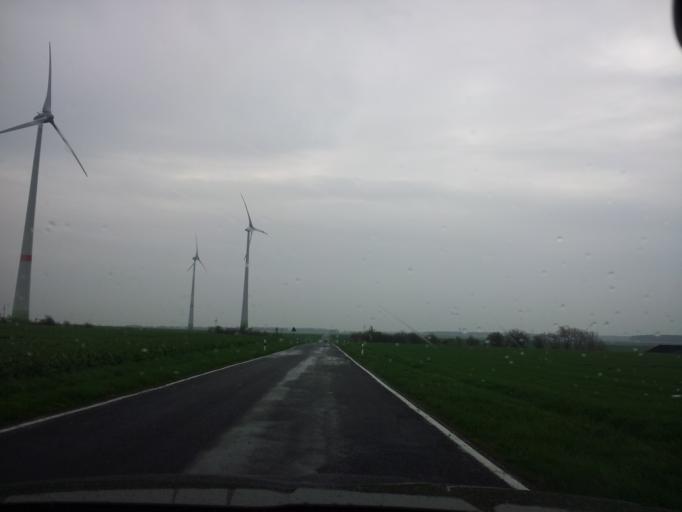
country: DE
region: Saxony-Anhalt
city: Kropstadt
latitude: 51.9876
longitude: 12.7975
